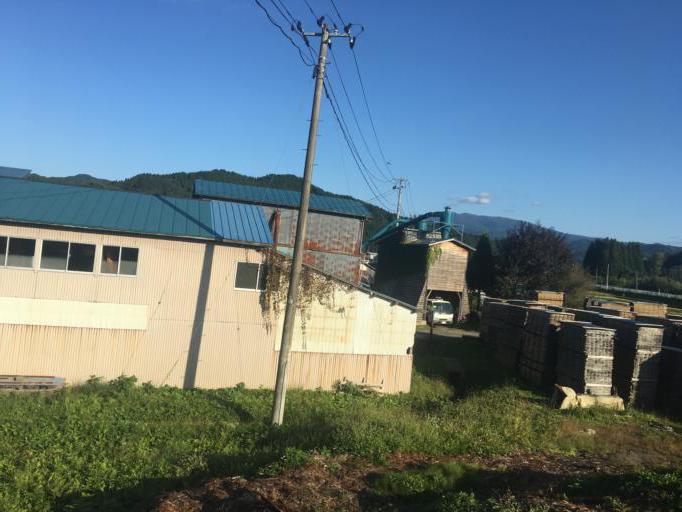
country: JP
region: Akita
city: Takanosu
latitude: 40.0572
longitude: 140.4162
